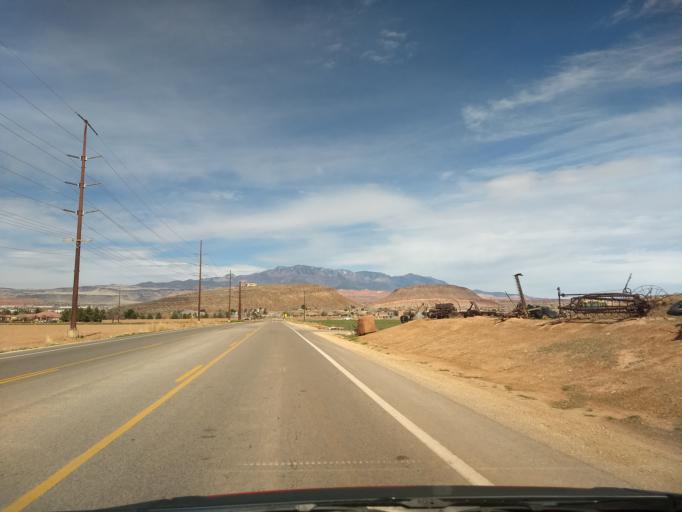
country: US
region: Utah
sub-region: Washington County
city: Washington
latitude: 37.0857
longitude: -113.4996
